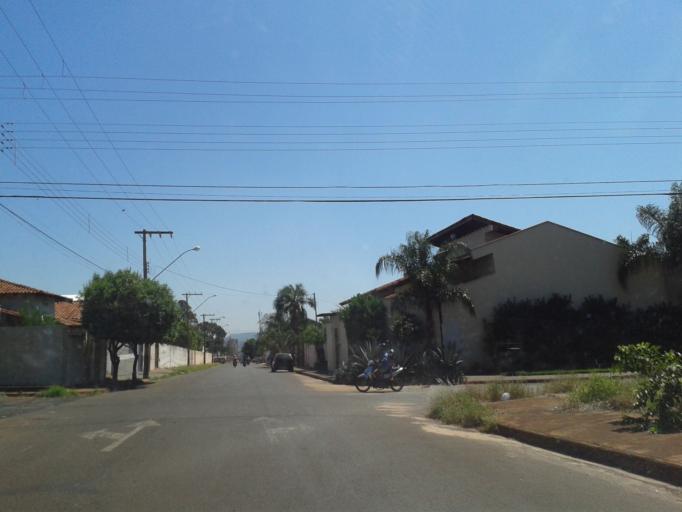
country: BR
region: Minas Gerais
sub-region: Ituiutaba
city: Ituiutaba
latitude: -18.9919
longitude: -49.4567
